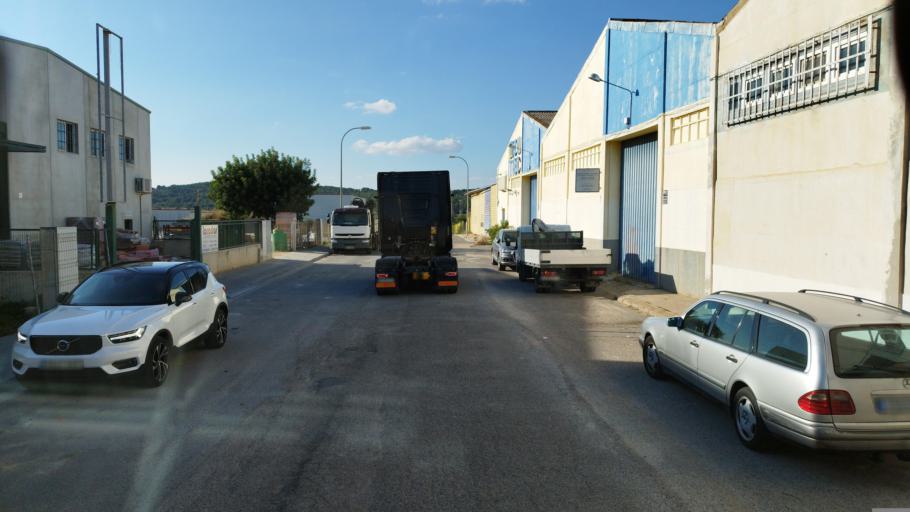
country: ES
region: Catalonia
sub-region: Provincia de Tarragona
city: Torredembarra
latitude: 41.1510
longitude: 1.3922
